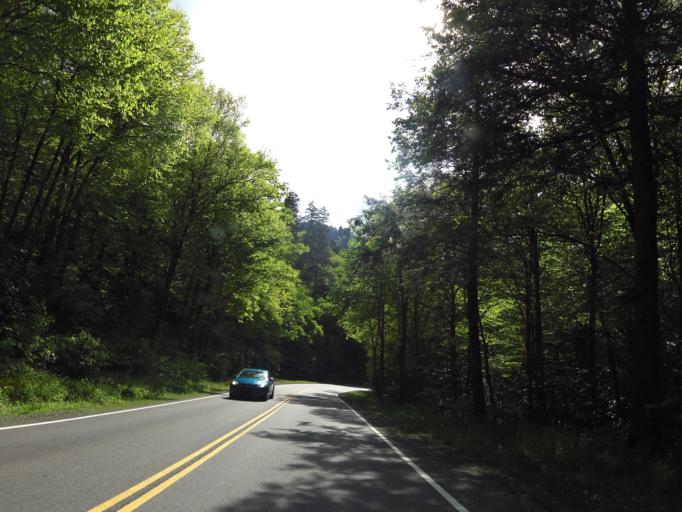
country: US
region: Tennessee
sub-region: Sevier County
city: Gatlinburg
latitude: 35.6187
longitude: -83.4300
